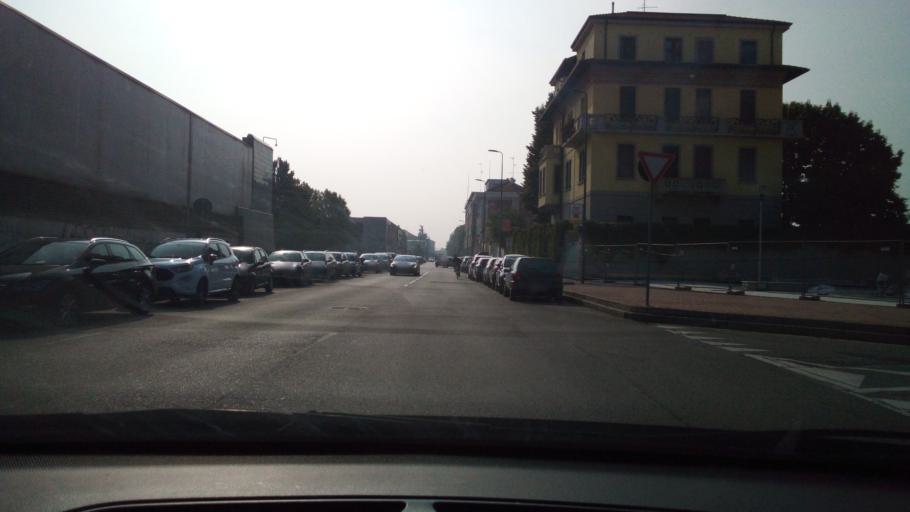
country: IT
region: Lombardy
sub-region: Citta metropolitana di Milano
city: Novegro-Tregarezzo-San Felice
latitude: 45.4798
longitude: 9.2458
